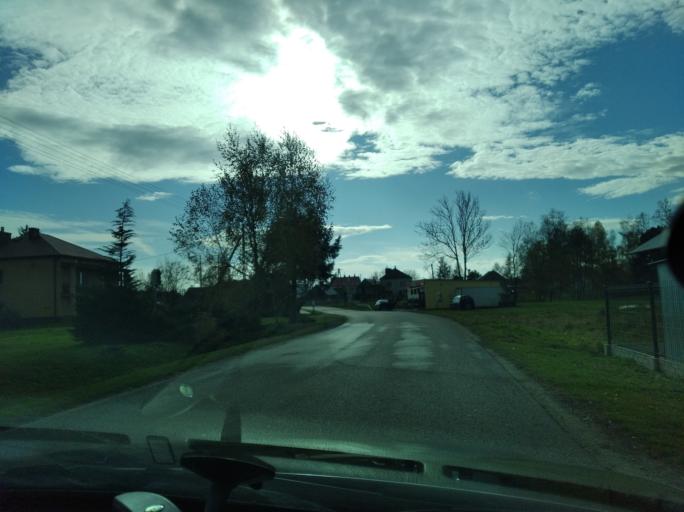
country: PL
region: Subcarpathian Voivodeship
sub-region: Powiat ropczycko-sedziszowski
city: Ostrow
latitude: 50.0941
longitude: 21.5545
